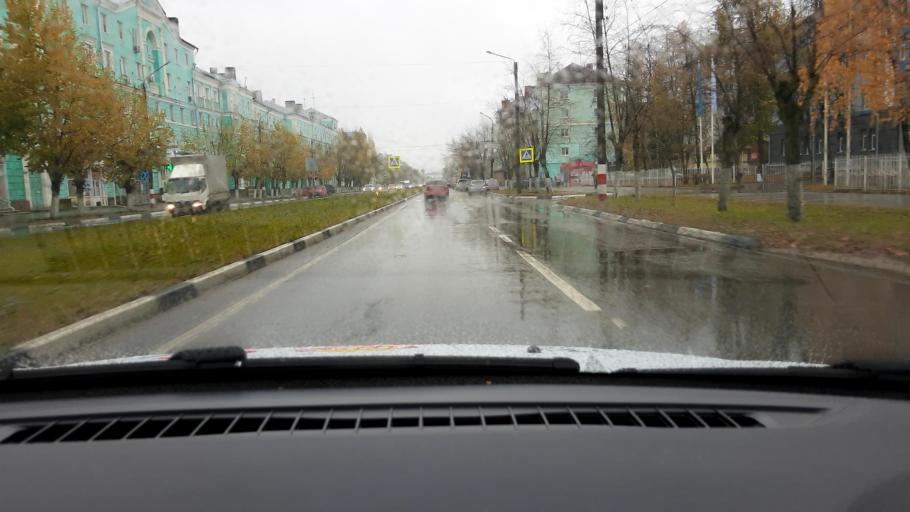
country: RU
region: Nizjnij Novgorod
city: Dzerzhinsk
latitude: 56.2411
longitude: 43.4476
